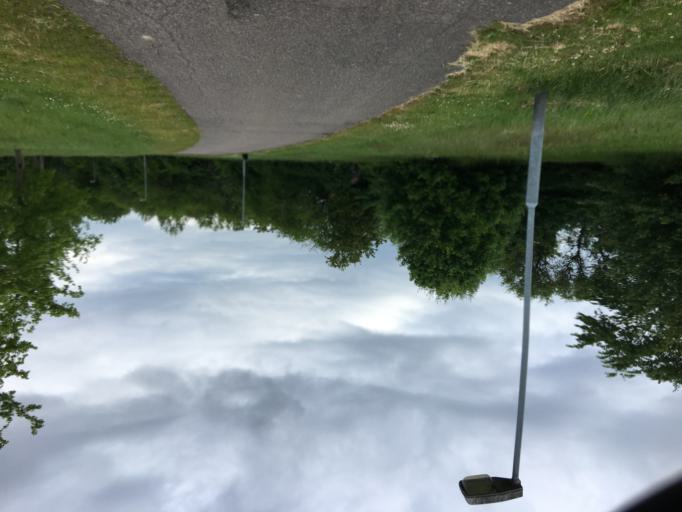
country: SE
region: Skane
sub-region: Malmo
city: Malmoe
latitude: 55.5775
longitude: 13.0466
